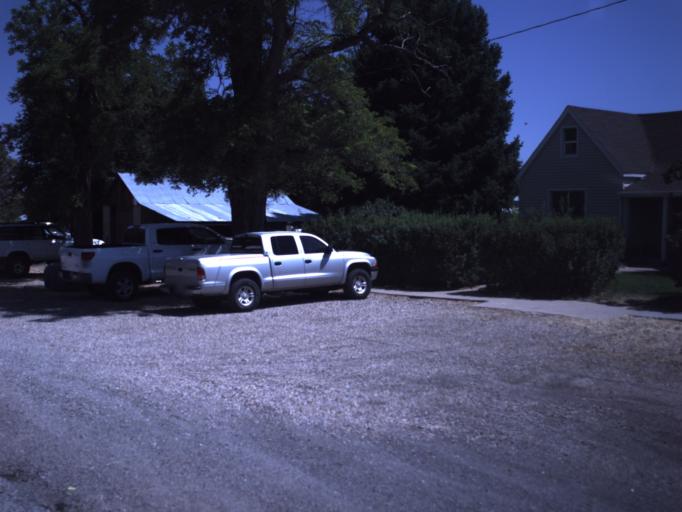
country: US
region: Utah
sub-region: Millard County
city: Delta
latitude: 39.3711
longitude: -112.3361
